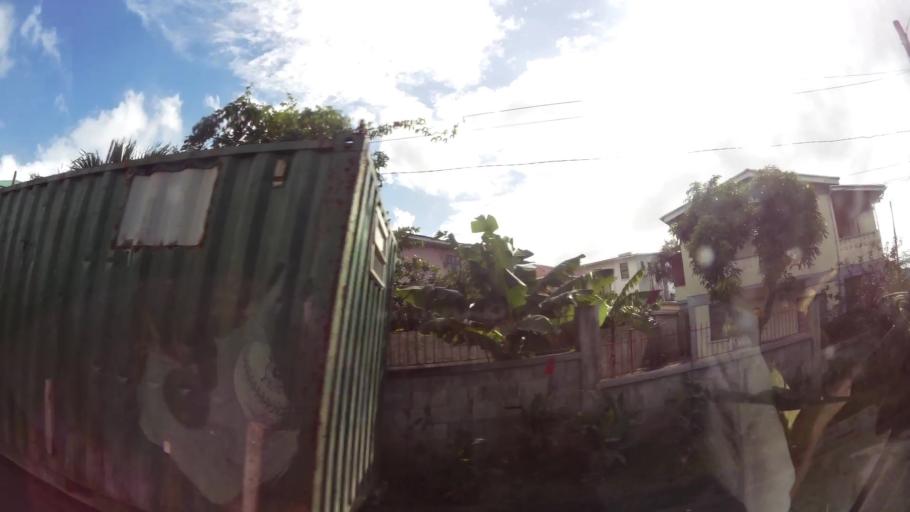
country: DM
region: Saint George
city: Roseau
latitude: 15.3056
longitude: -61.3830
